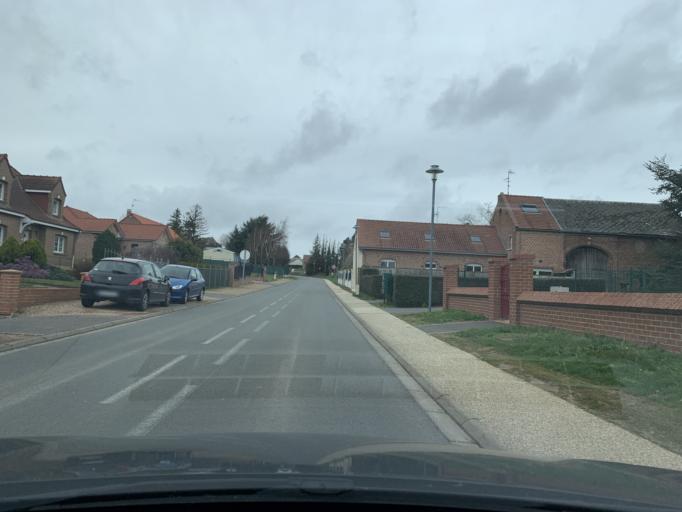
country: FR
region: Nord-Pas-de-Calais
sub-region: Departement du Nord
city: Cambrai
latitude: 50.1532
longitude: 3.2773
